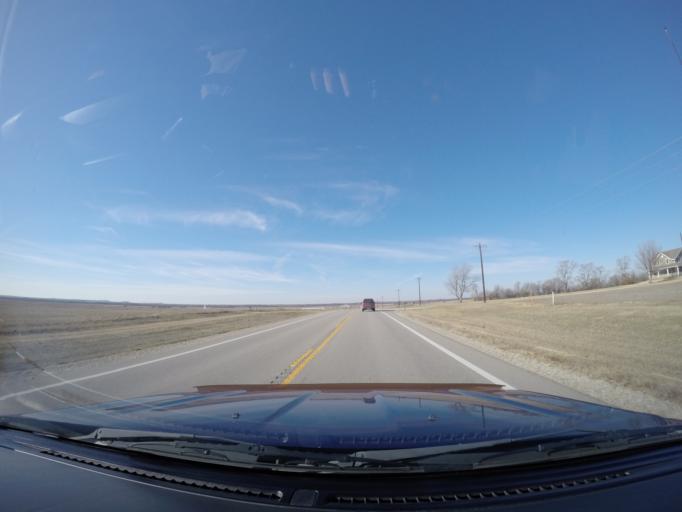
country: US
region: Kansas
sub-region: Clay County
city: Clay Center
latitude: 39.3799
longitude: -97.1998
